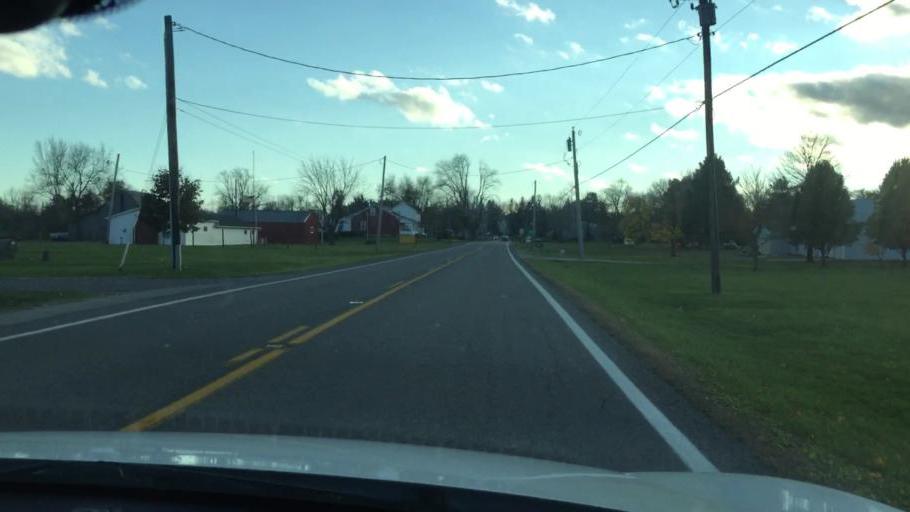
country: US
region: Ohio
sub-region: Champaign County
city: North Lewisburg
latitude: 40.1787
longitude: -83.5252
